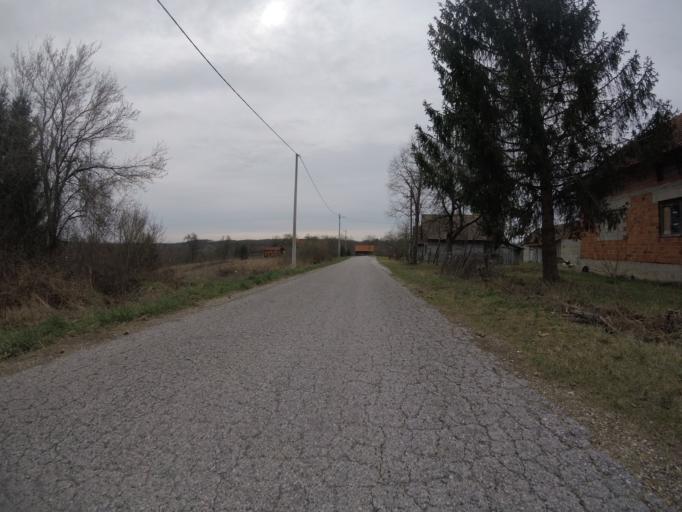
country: HR
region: Zagrebacka
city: Lukavec
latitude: 45.5704
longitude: 15.9629
